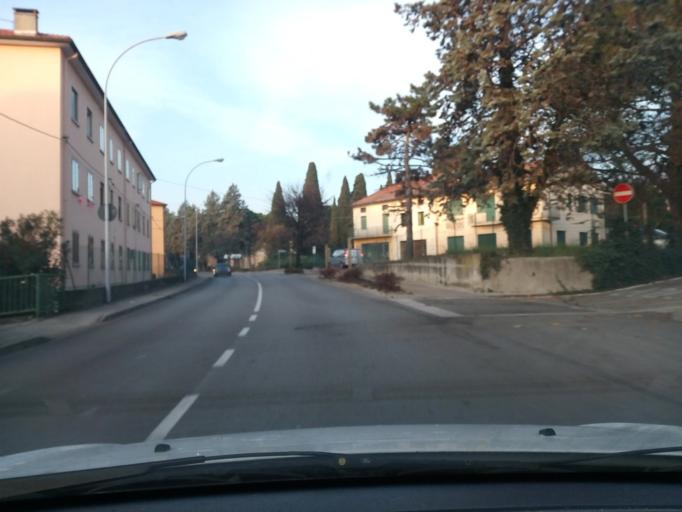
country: IT
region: Veneto
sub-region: Provincia di Vicenza
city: Schio
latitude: 45.7152
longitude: 11.3722
